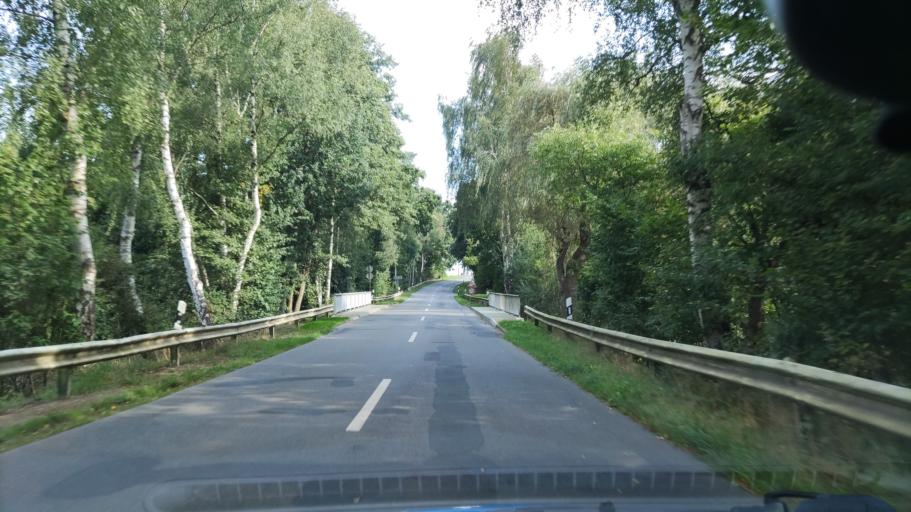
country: DE
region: Lower Saxony
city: Gerdau
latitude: 52.9727
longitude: 10.3741
